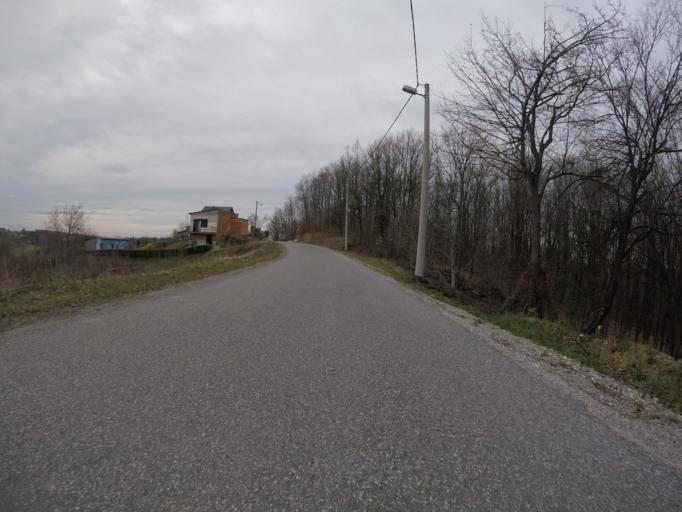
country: HR
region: Grad Zagreb
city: Strmec
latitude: 45.6306
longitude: 15.9352
